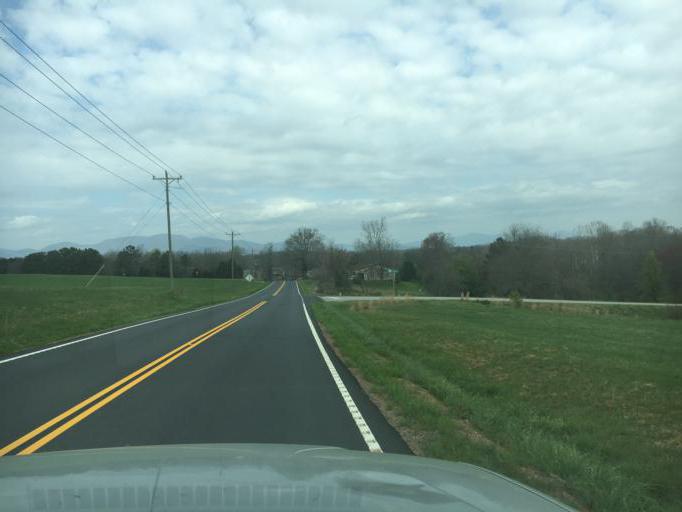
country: US
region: South Carolina
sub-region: Spartanburg County
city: Inman Mills
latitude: 35.0808
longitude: -82.1880
